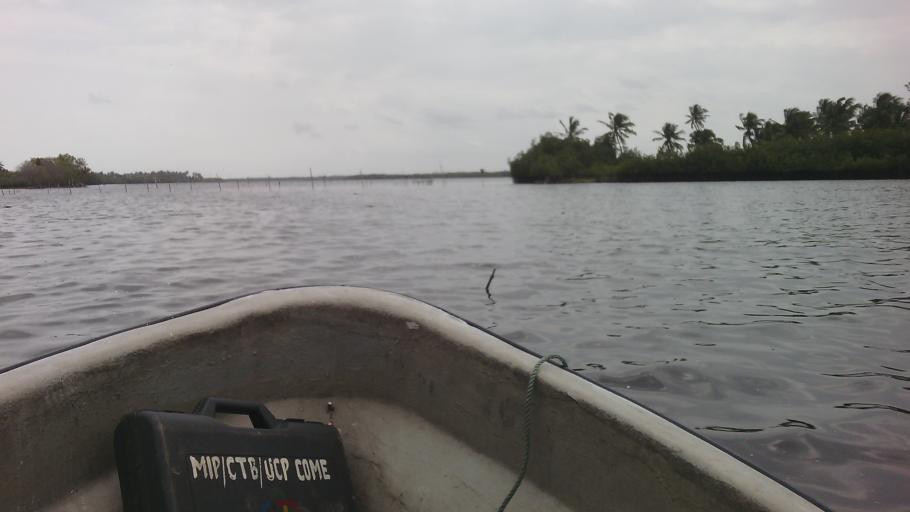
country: BJ
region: Atlantique
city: Ouidah
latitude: 6.3079
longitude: 1.9791
